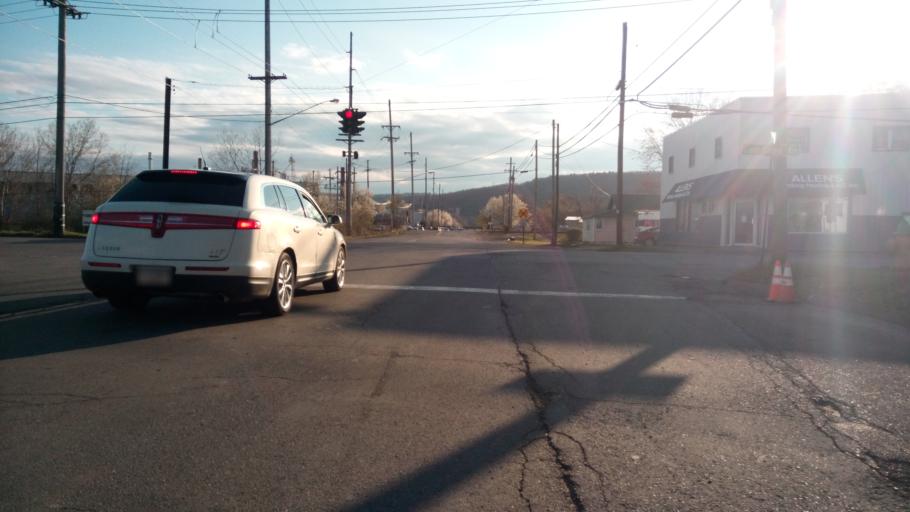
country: US
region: New York
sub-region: Chemung County
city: Elmira Heights
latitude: 42.1219
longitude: -76.8157
